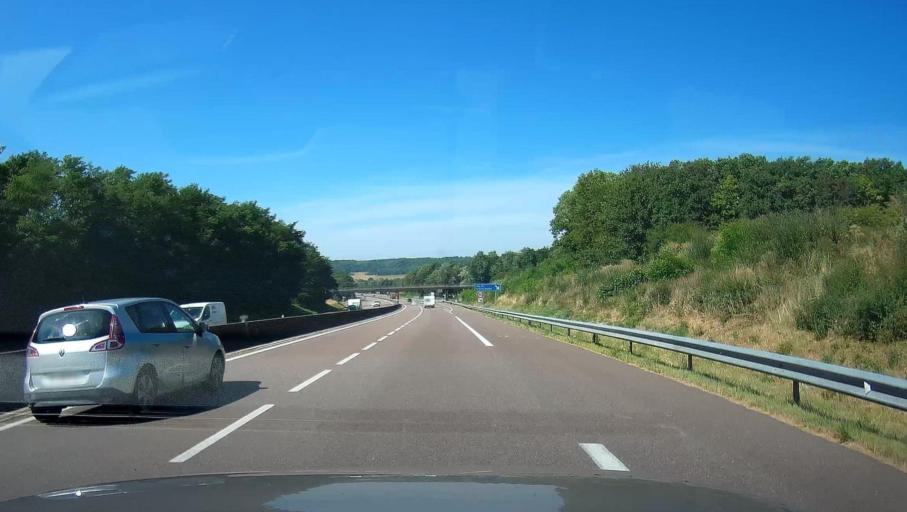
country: FR
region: Champagne-Ardenne
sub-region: Departement de la Haute-Marne
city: Rolampont
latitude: 47.9462
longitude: 5.3077
